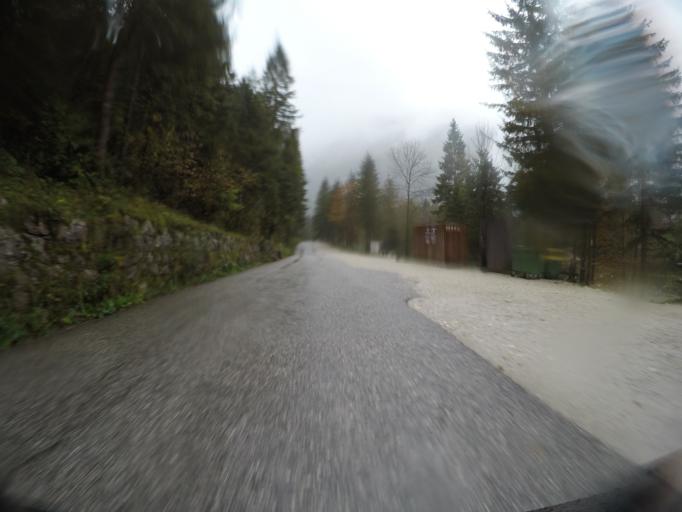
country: SI
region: Bovec
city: Bovec
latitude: 46.3348
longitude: 13.6456
